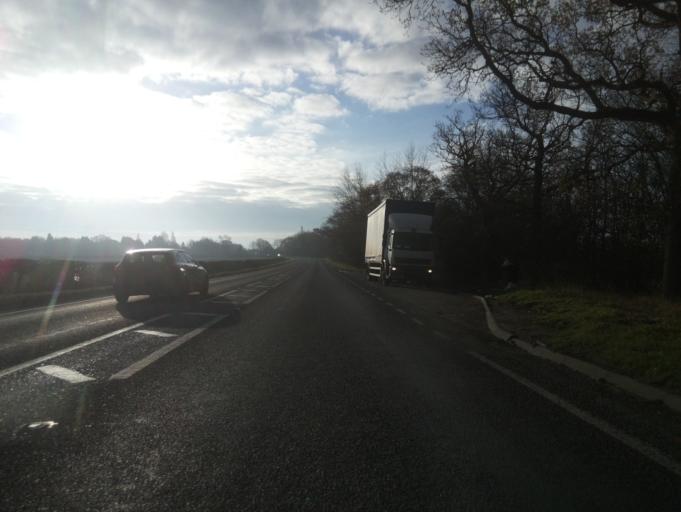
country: GB
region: England
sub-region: City and Borough of Birmingham
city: Sutton Coldfield
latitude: 52.5842
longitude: -1.7791
